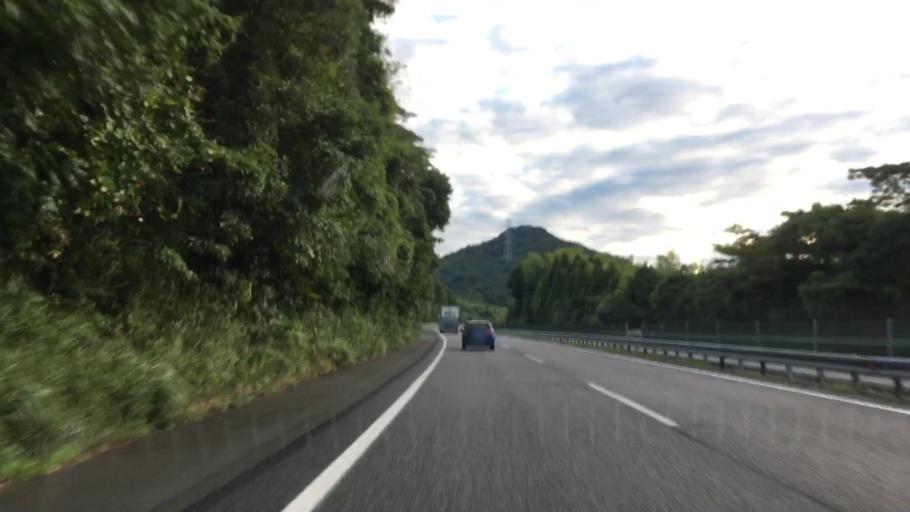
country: JP
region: Yamaguchi
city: Shimonoseki
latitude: 34.0433
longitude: 130.9873
